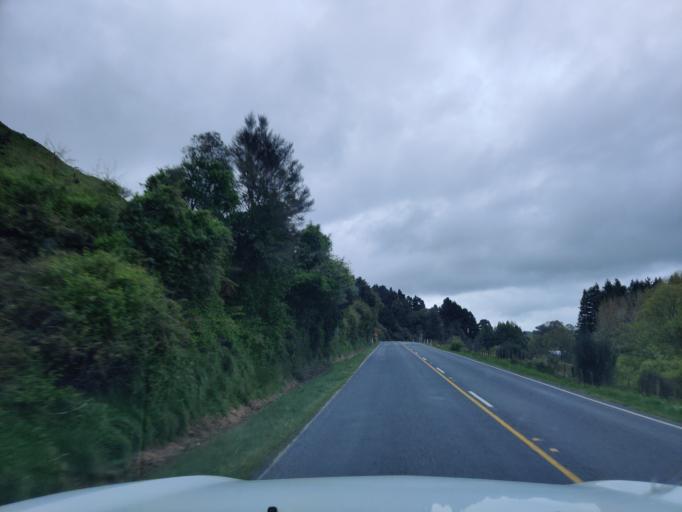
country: NZ
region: Waikato
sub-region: Otorohanga District
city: Otorohanga
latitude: -38.6116
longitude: 175.2182
